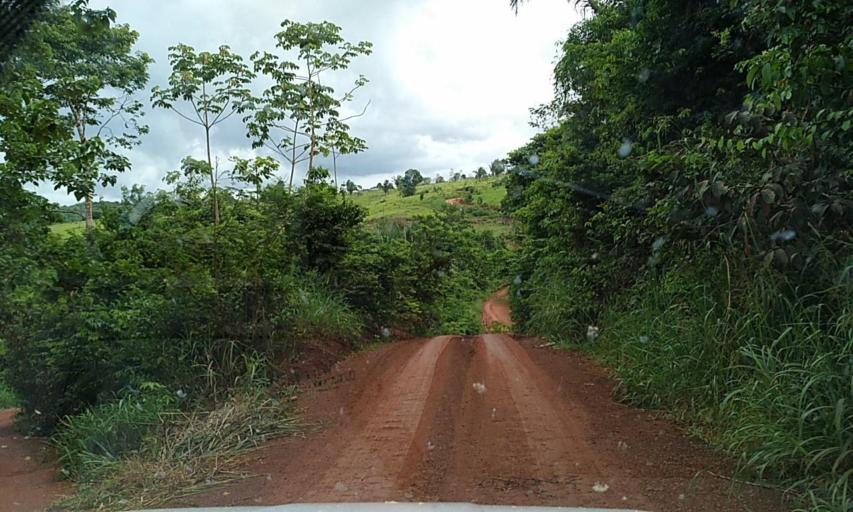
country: BR
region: Para
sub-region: Altamira
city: Altamira
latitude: -3.3203
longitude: -52.6845
